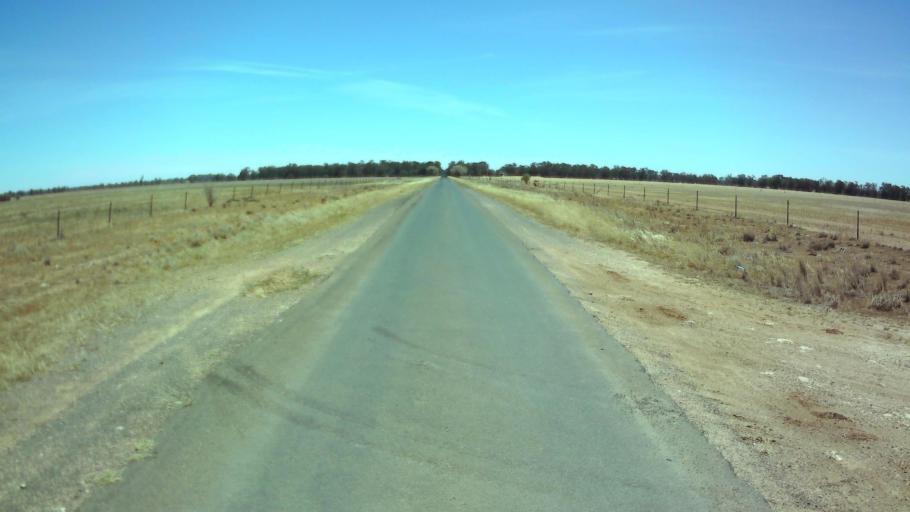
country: AU
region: New South Wales
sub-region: Weddin
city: Grenfell
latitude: -33.8597
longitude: 147.6940
